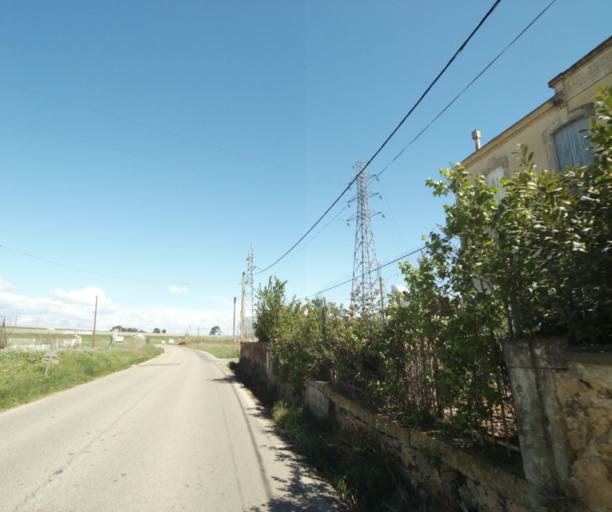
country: FR
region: Languedoc-Roussillon
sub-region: Departement de l'Herault
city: Villeneuve-les-Maguelone
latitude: 43.5654
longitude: 3.8692
